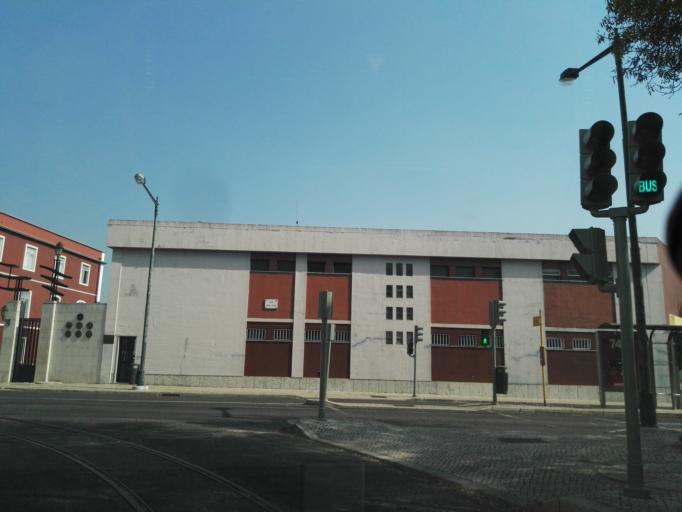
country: PT
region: Lisbon
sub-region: Lisbon
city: Lisbon
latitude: 38.7262
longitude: -9.1409
